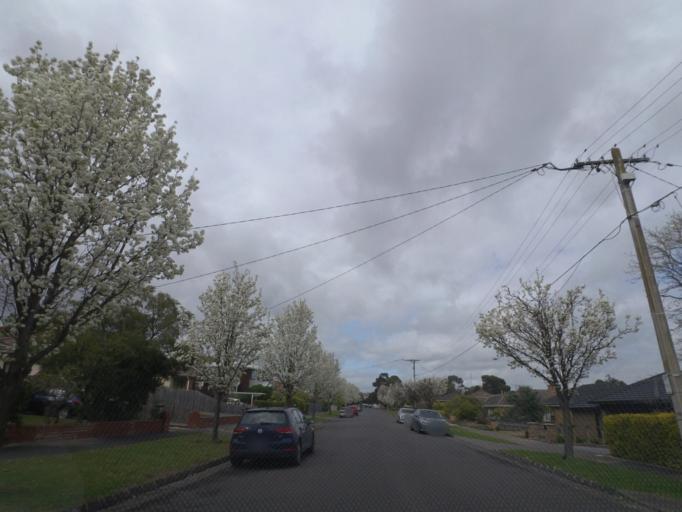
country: AU
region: Victoria
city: Mitcham
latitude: -37.8150
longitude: 145.1894
